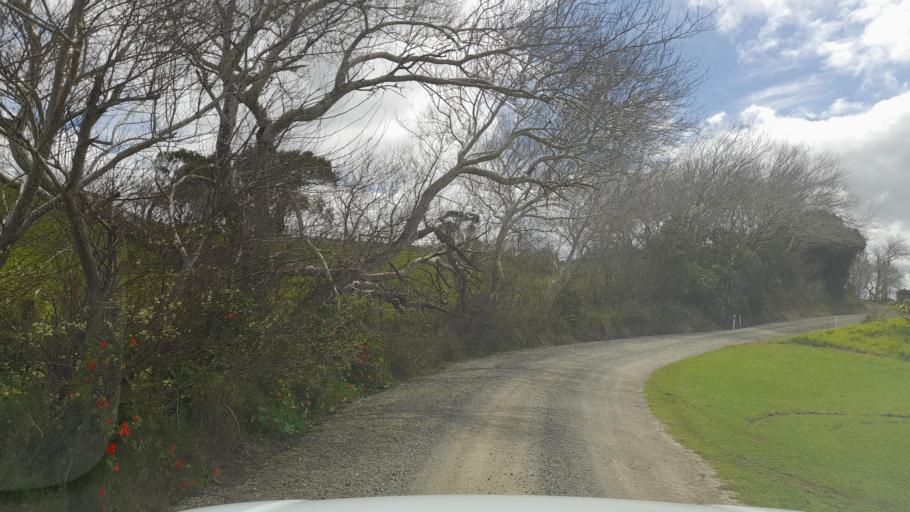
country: NZ
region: Auckland
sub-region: Auckland
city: Wellsford
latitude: -36.2208
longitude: 174.3205
